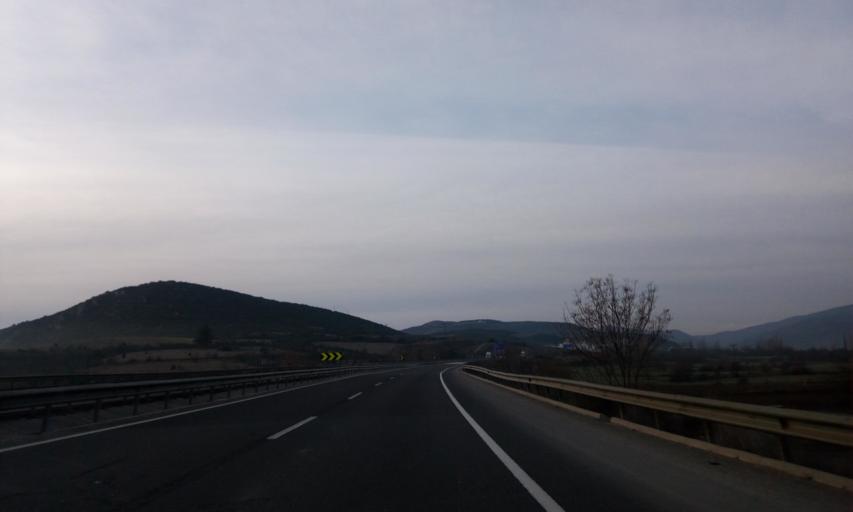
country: TR
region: Bilecik
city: Bilecik
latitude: 40.1428
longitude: 30.0263
